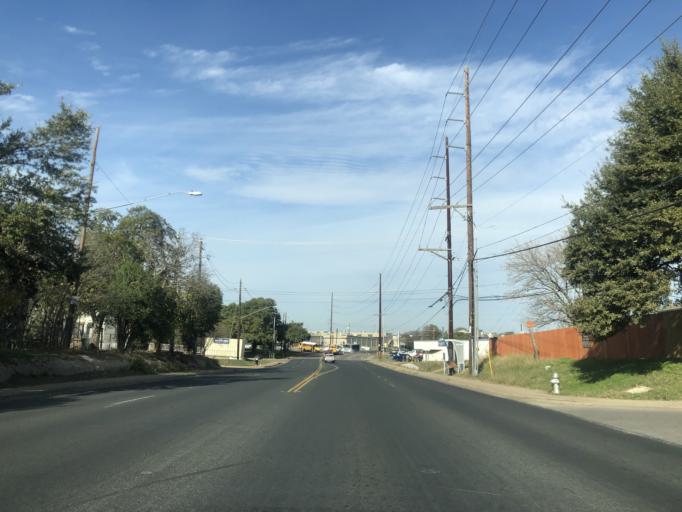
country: US
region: Texas
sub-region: Travis County
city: Onion Creek
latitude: 30.1873
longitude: -97.7681
